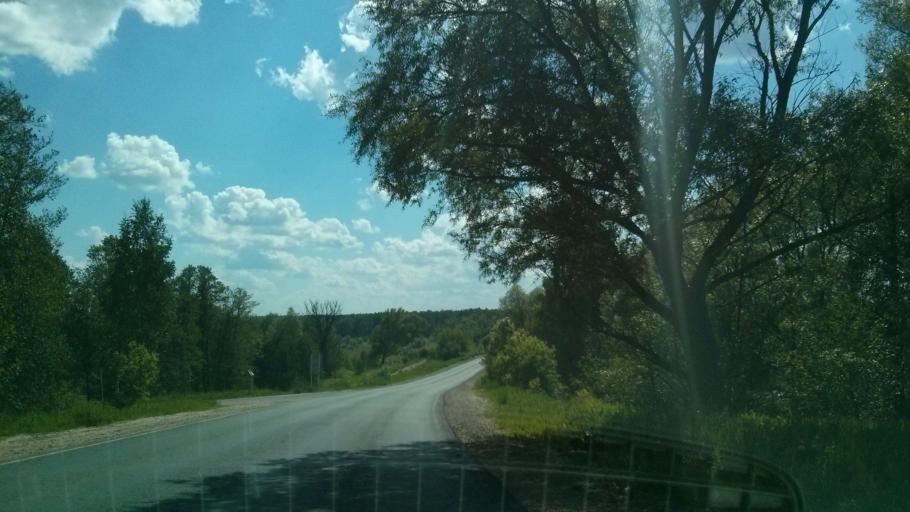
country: RU
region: Vladimir
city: Murom
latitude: 55.5256
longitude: 41.9541
